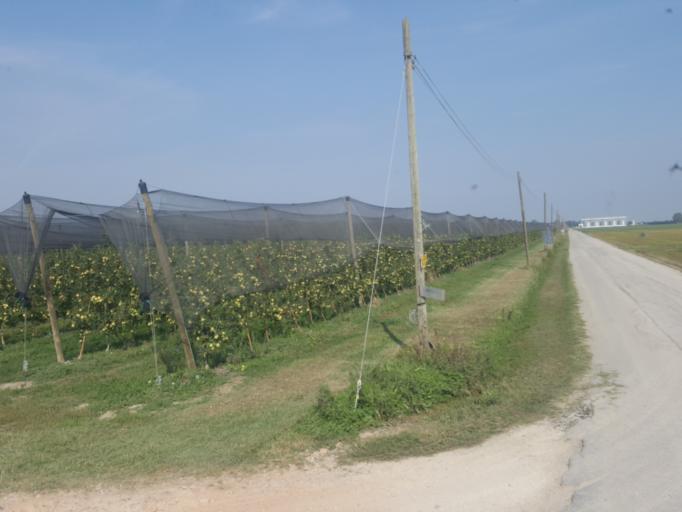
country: IT
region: Emilia-Romagna
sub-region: Provincia di Ravenna
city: Voltana
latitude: 44.5765
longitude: 11.9446
